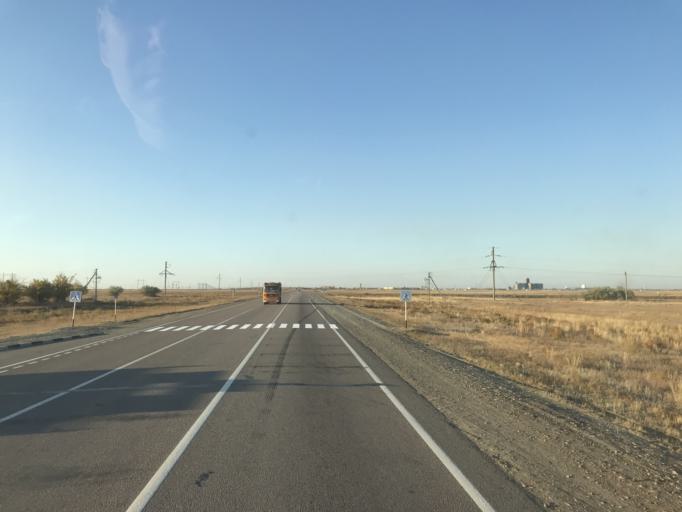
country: KZ
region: Pavlodar
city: Leninskiy
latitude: 52.2160
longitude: 76.7628
